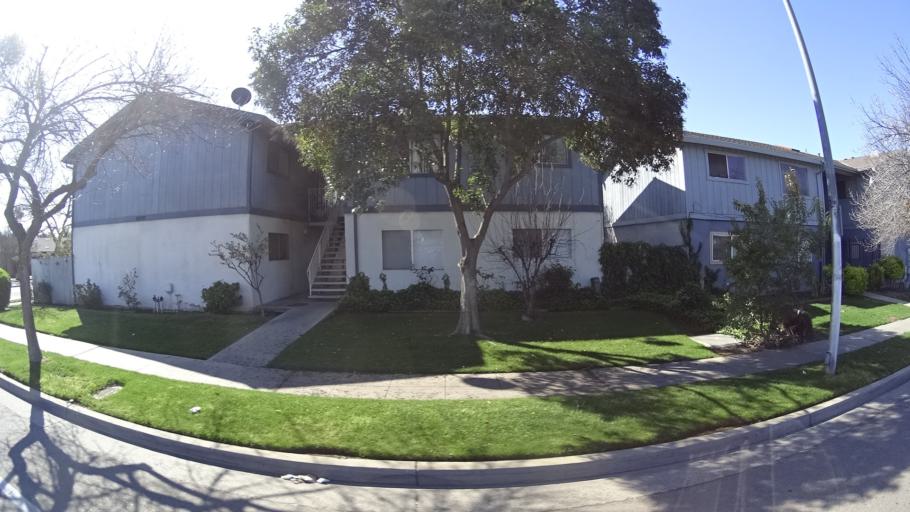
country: US
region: California
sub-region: Fresno County
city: Fresno
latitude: 36.7792
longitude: -119.8339
